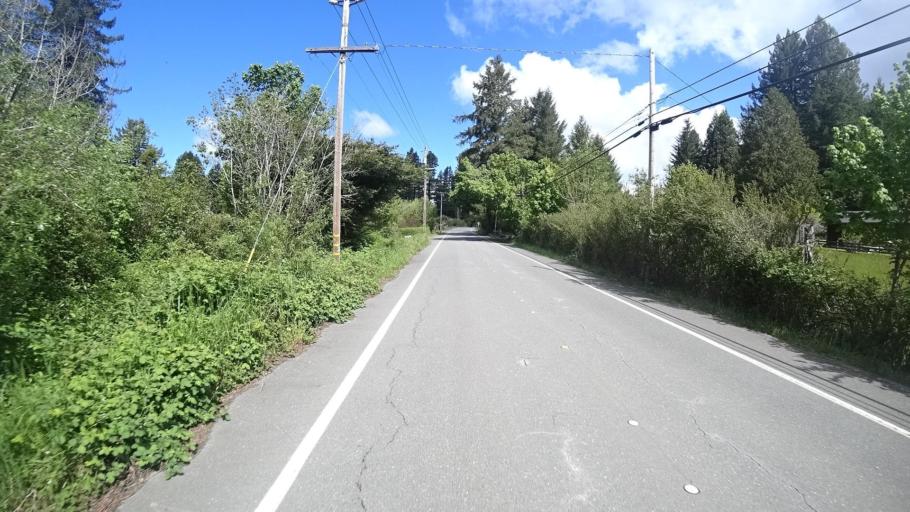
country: US
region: California
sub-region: Humboldt County
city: McKinleyville
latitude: 40.9524
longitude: -124.0330
